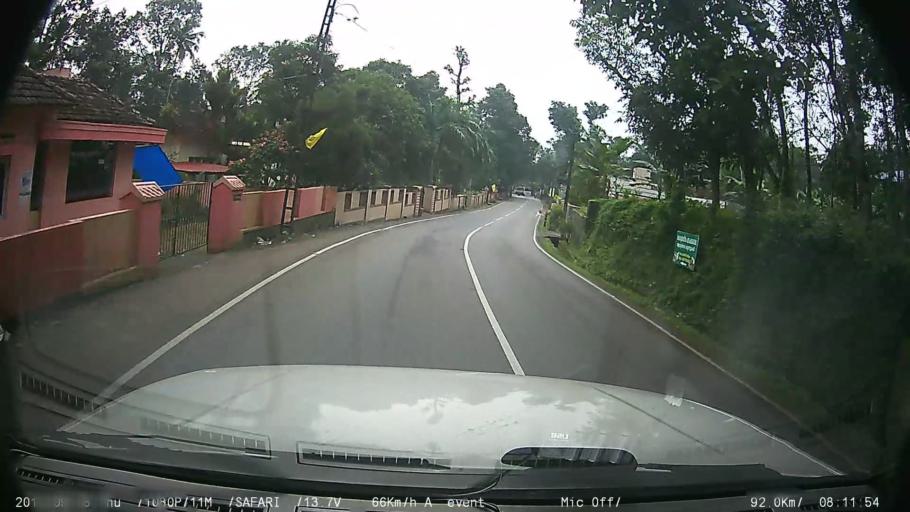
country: IN
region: Kerala
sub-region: Kottayam
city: Kottayam
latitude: 9.6078
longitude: 76.5974
